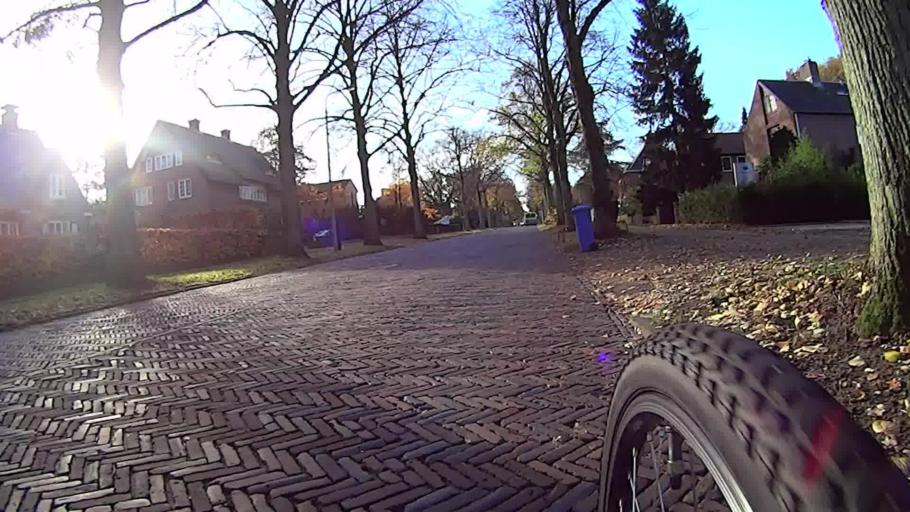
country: NL
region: Utrecht
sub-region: Gemeente Amersfoort
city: Amersfoort
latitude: 52.1513
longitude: 5.3720
